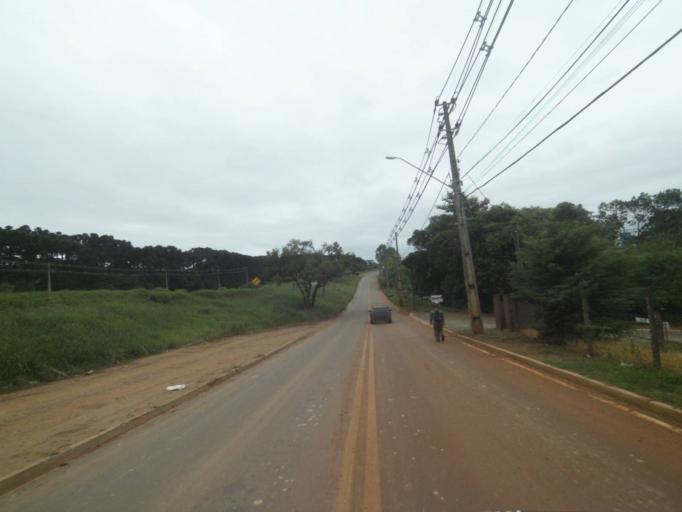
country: BR
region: Parana
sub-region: Telemaco Borba
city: Telemaco Borba
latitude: -24.3632
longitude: -50.6587
